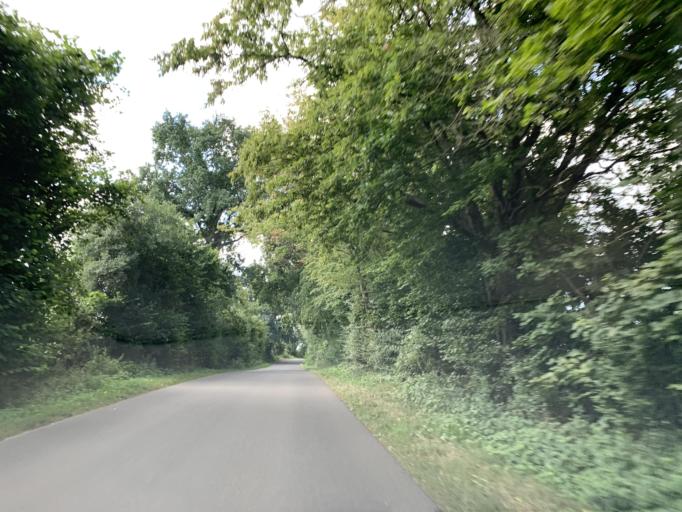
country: DE
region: Mecklenburg-Vorpommern
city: Carpin
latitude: 53.3727
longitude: 13.2587
